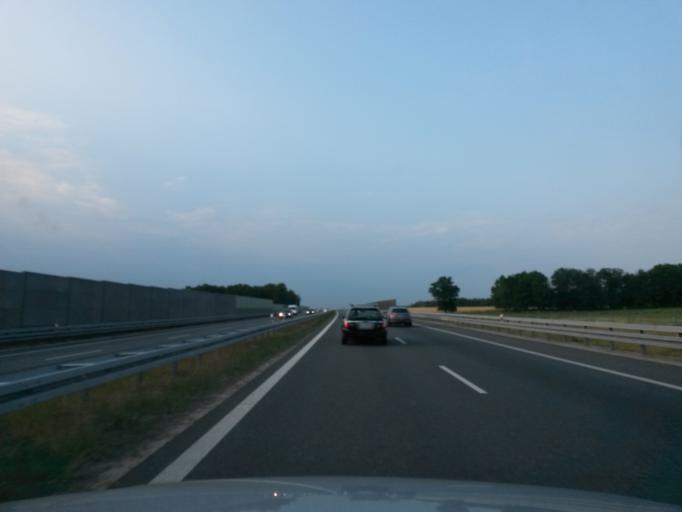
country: PL
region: Lower Silesian Voivodeship
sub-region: Powiat olesnicki
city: Twardogora
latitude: 51.2635
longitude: 17.5481
